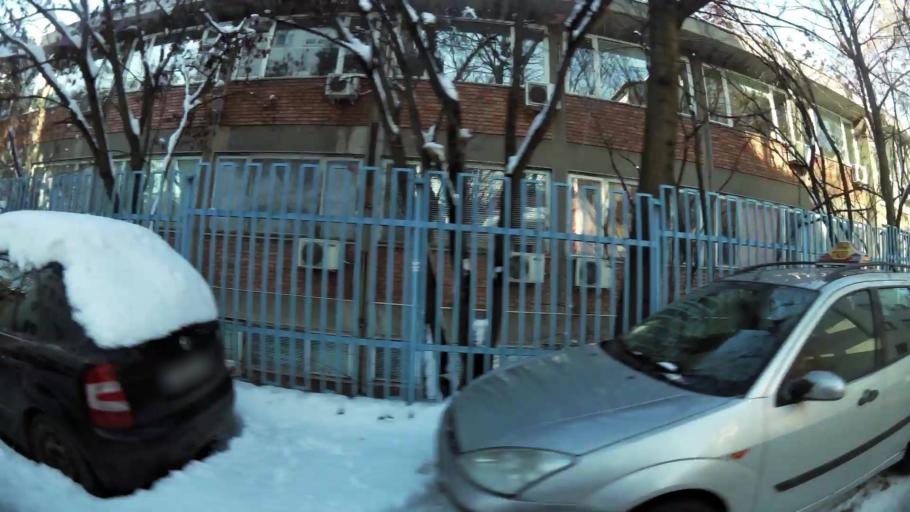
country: RS
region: Central Serbia
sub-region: Belgrade
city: Palilula
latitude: 44.8159
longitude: 20.5164
